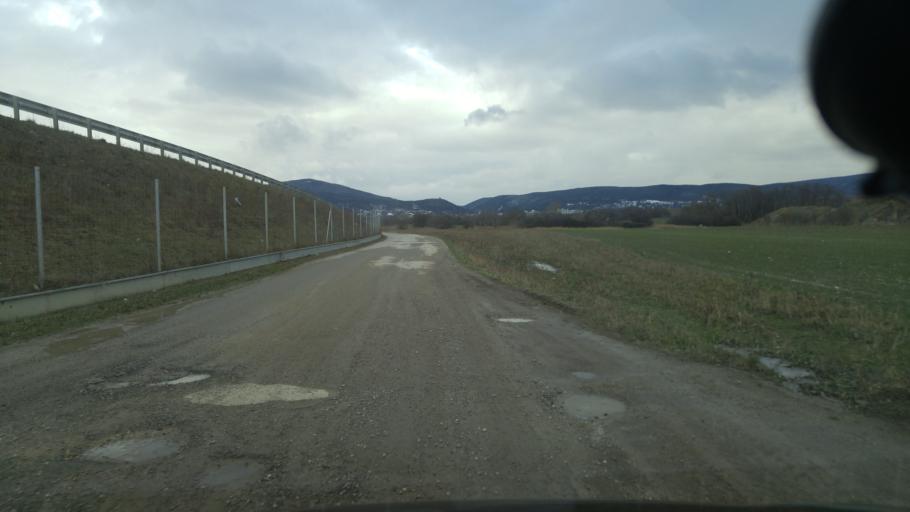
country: AT
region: Lower Austria
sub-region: Politischer Bezirk Baden
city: Kottingbrunn
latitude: 47.9735
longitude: 16.2410
